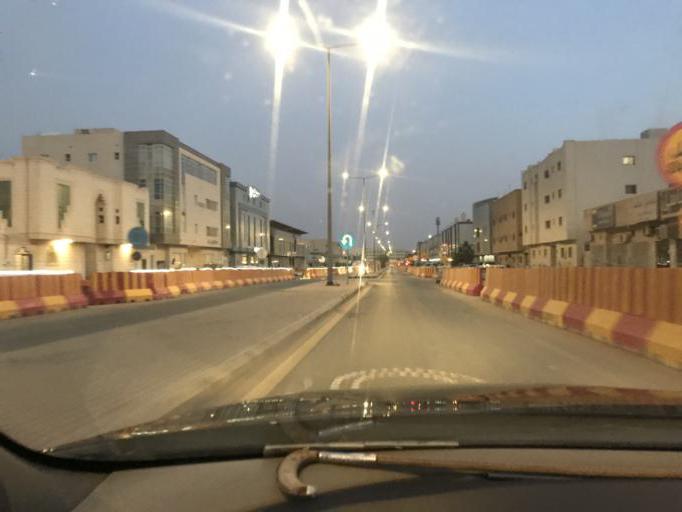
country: SA
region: Ar Riyad
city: Riyadh
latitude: 24.8017
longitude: 46.7072
